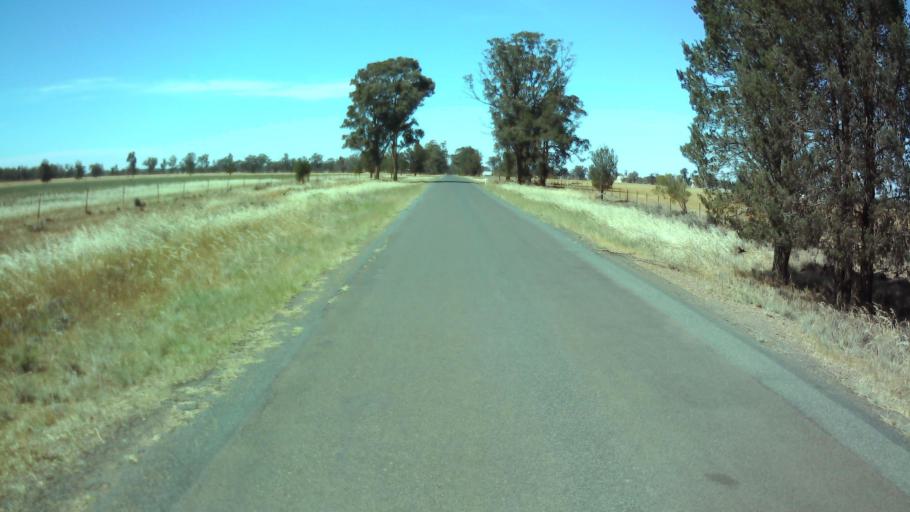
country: AU
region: New South Wales
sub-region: Weddin
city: Grenfell
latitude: -34.1048
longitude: 147.8869
